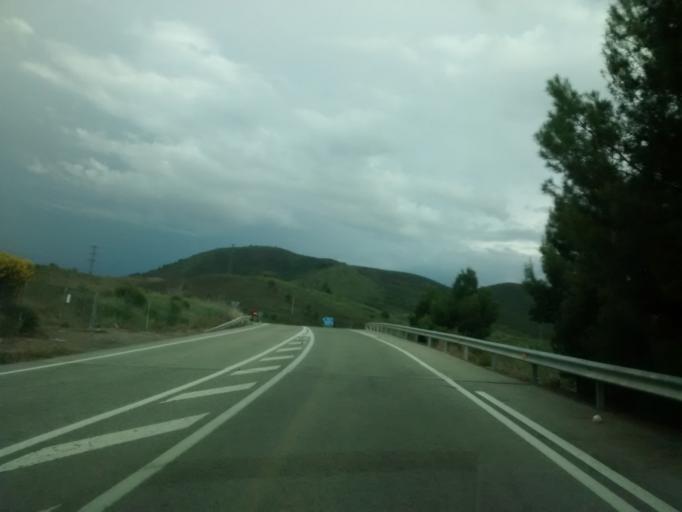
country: ES
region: Aragon
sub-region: Provincia de Zaragoza
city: Ateca
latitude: 41.3221
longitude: -1.7946
